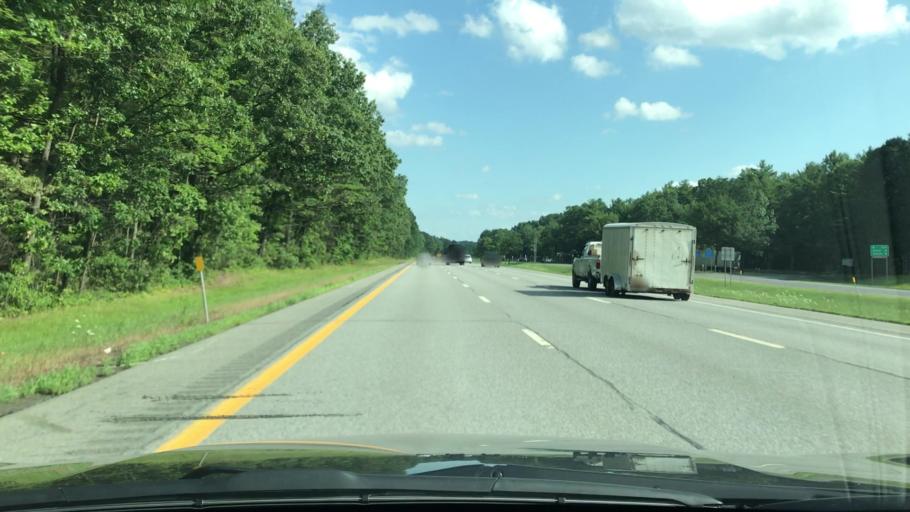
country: US
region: New York
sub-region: Warren County
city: West Glens Falls
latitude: 43.2772
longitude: -73.6780
